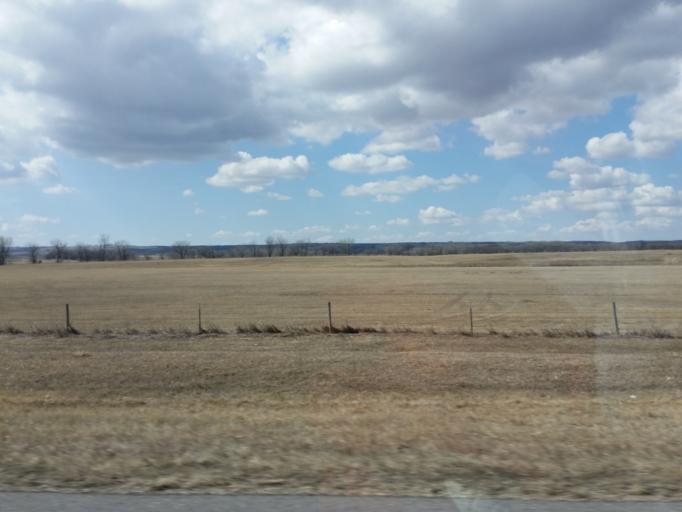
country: US
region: South Dakota
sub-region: Roberts County
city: Sisseton
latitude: 45.5316
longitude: -96.9896
